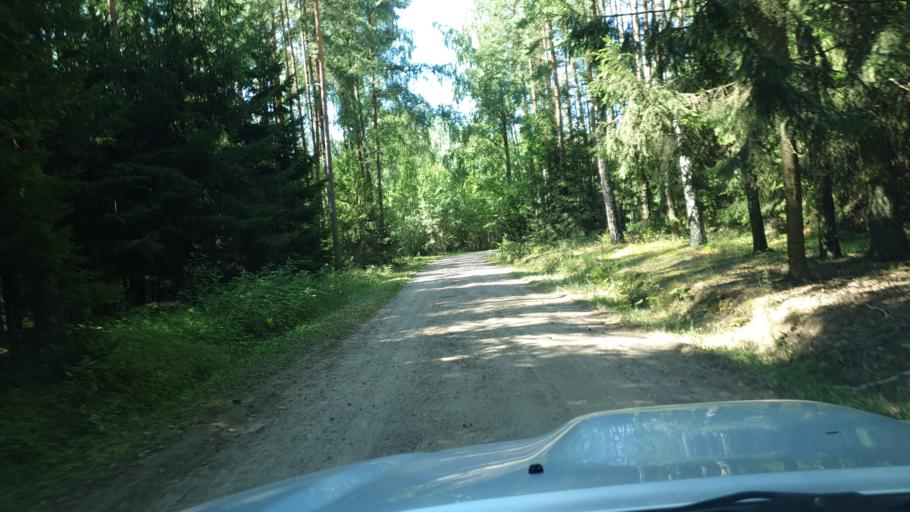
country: LT
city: Sirvintos
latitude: 54.9136
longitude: 24.9265
